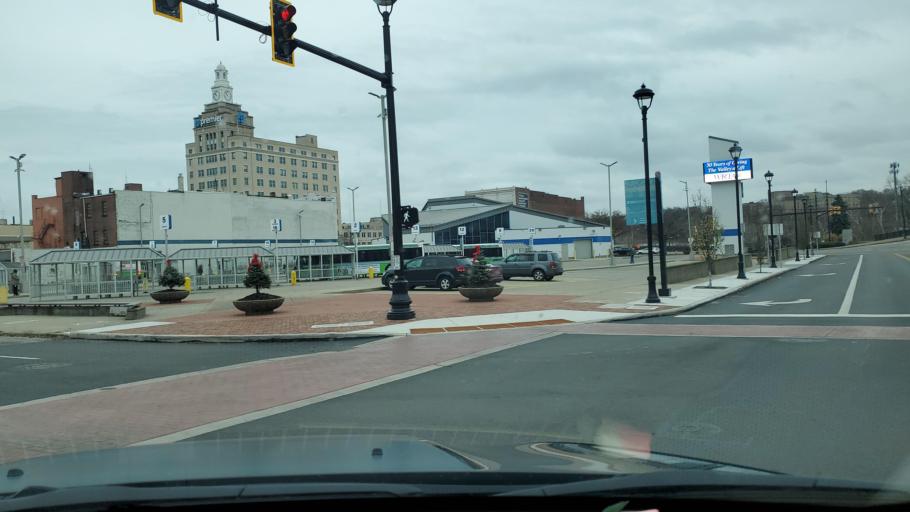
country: US
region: Ohio
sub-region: Mahoning County
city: Youngstown
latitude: 41.1036
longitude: -80.6545
